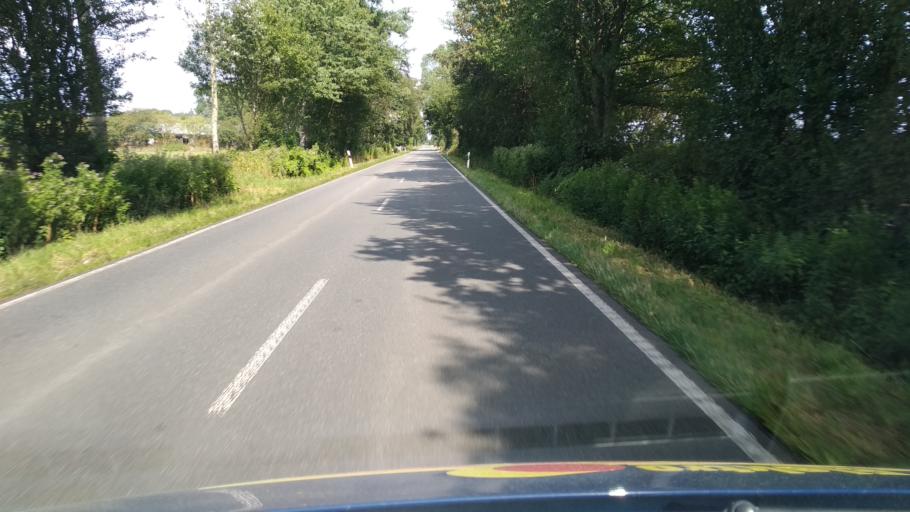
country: DE
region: Schleswig-Holstein
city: Brekendorf
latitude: 54.4246
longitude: 9.6194
